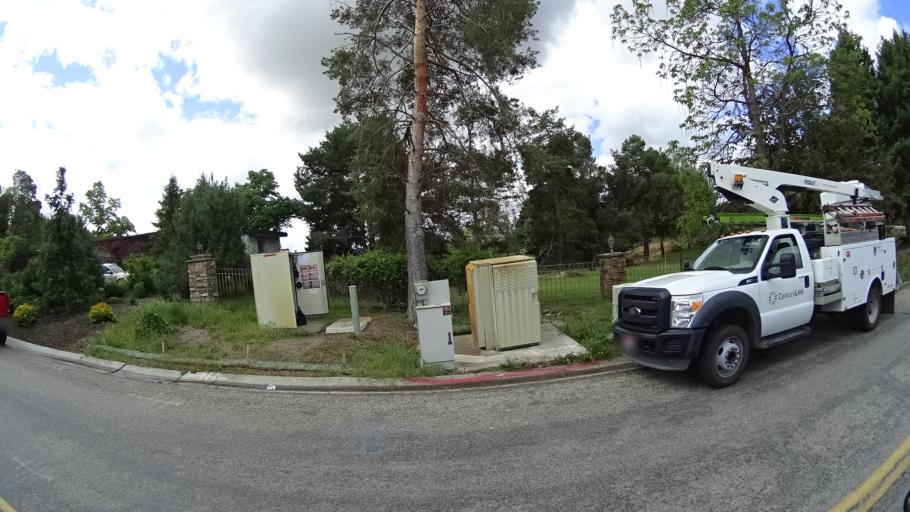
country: US
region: Idaho
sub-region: Ada County
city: Boise
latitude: 43.6459
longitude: -116.1881
